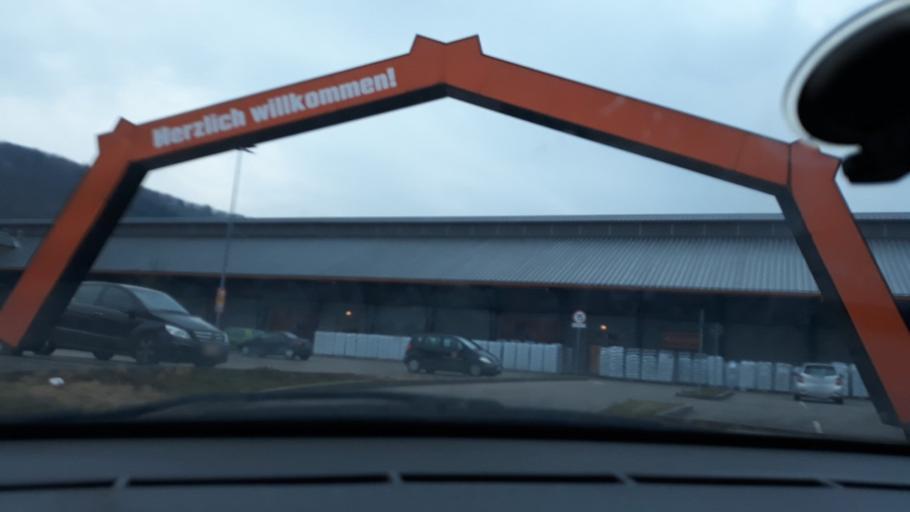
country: DE
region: Saarland
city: Sankt Ingbert
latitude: 49.2713
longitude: 7.1316
